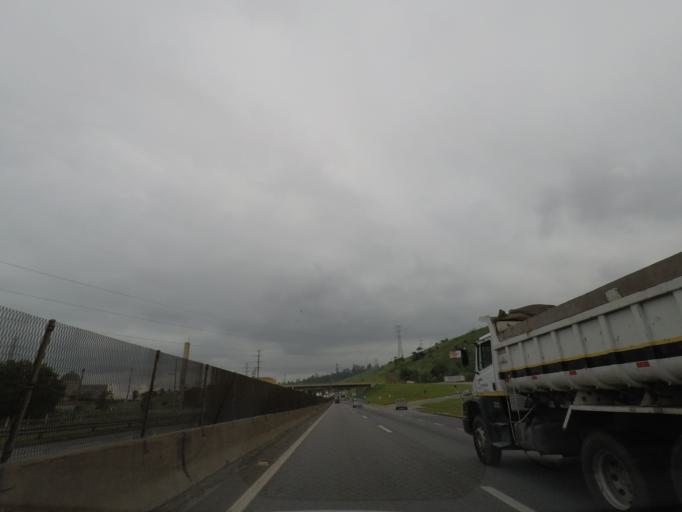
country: BR
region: Sao Paulo
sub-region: Aparecida
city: Aparecida
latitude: -22.8600
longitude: -45.2345
